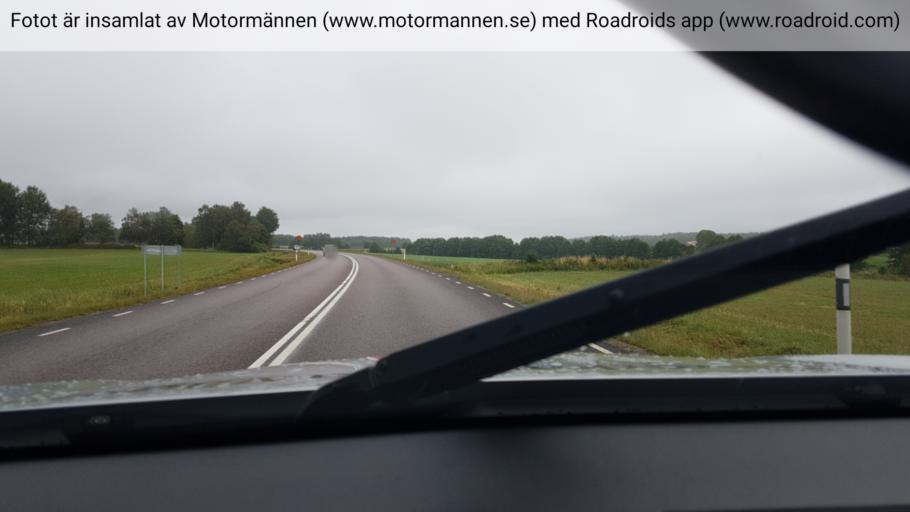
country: SE
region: Vaestra Goetaland
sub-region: Lerums Kommun
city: Olstorp
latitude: 57.8271
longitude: 12.2468
